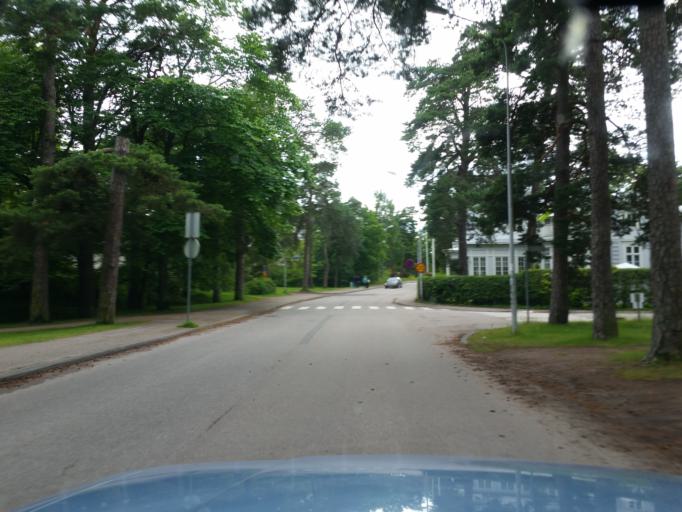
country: FI
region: Uusimaa
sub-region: Raaseporin
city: Hanko
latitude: 59.8240
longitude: 22.9764
